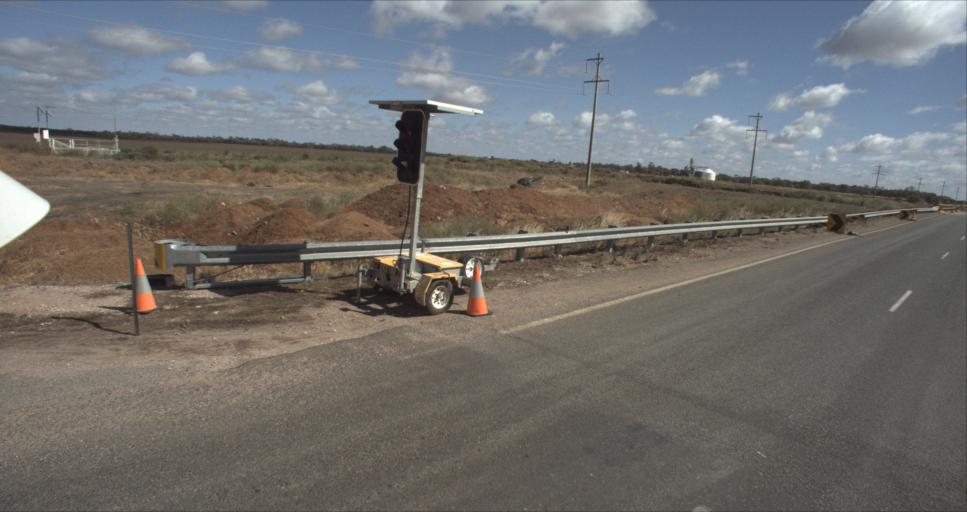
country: AU
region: New South Wales
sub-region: Murrumbidgee Shire
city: Darlington Point
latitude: -34.5538
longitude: 146.1702
